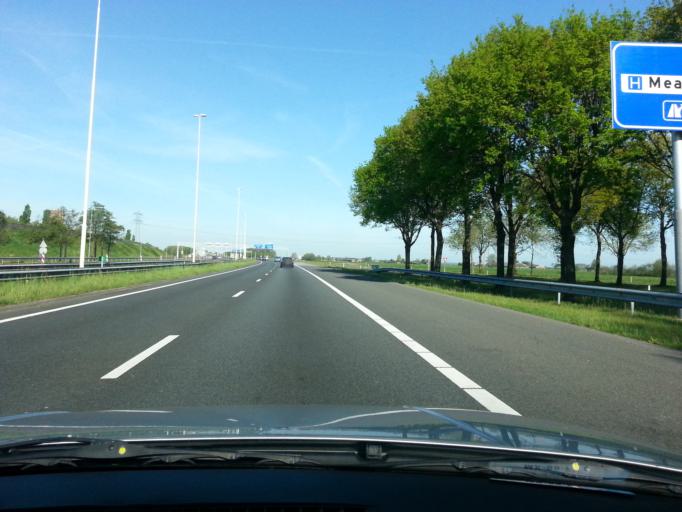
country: NL
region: Utrecht
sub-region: Gemeente Amersfoort
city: Hoogland
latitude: 52.2055
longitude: 5.3832
